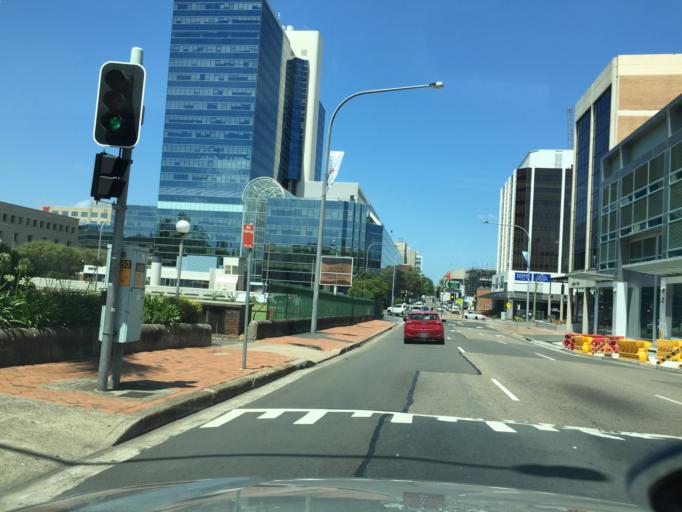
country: AU
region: New South Wales
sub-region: Parramatta
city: City of Parramatta
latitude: -33.8141
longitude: 150.9988
